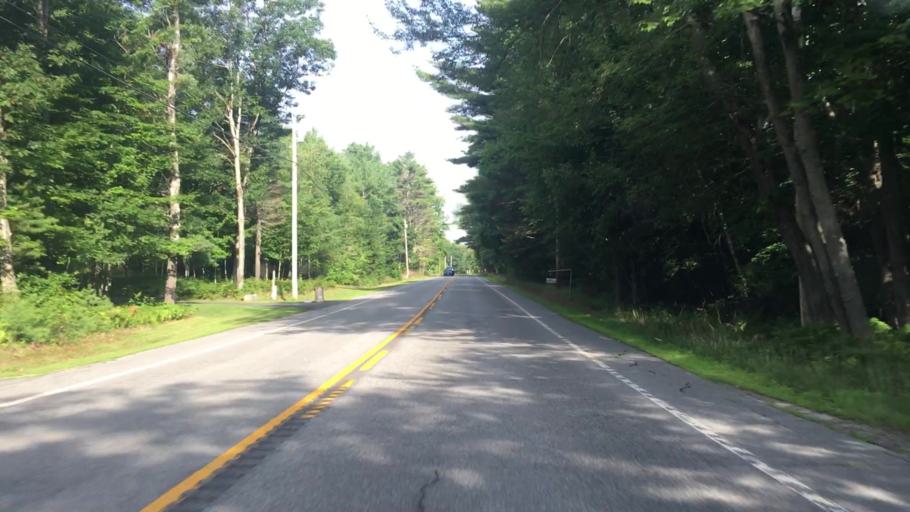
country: US
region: Maine
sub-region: York County
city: Cornish
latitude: 43.7791
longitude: -70.7484
